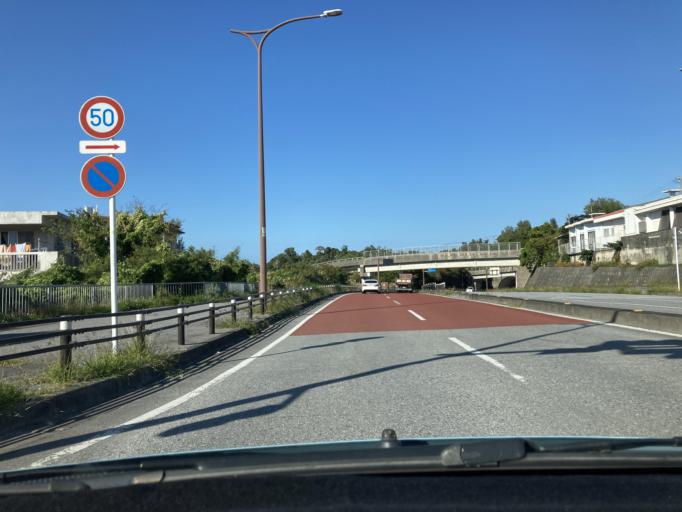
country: JP
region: Okinawa
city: Ishikawa
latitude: 26.4204
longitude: 127.8151
